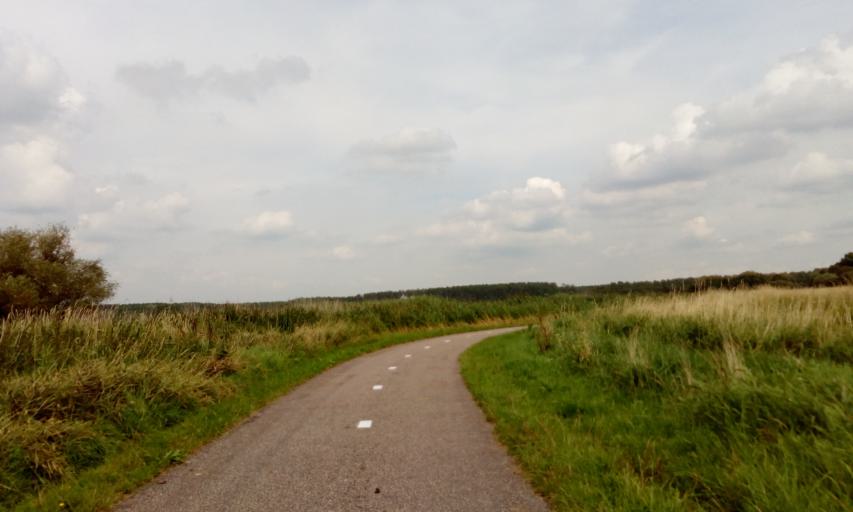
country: NL
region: South Holland
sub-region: Gemeente Pijnacker-Nootdorp
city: Pijnacker
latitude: 52.0345
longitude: 4.4371
